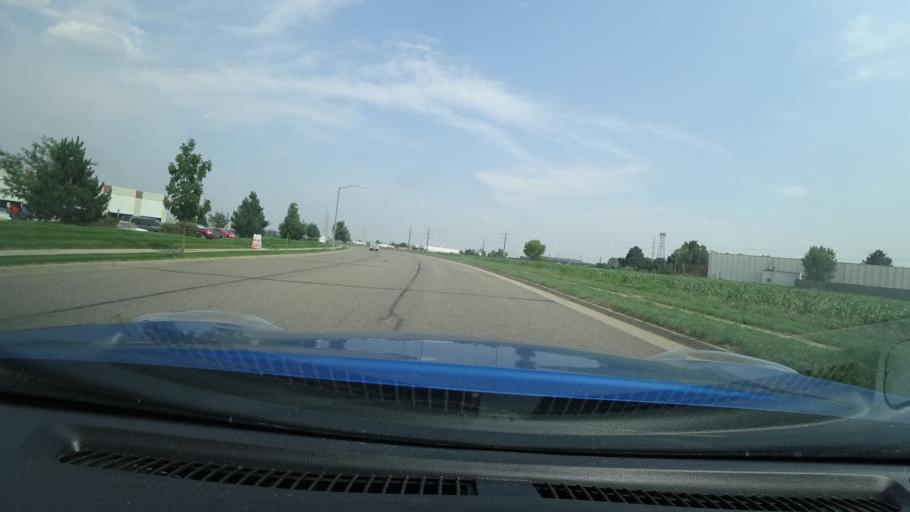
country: US
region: Colorado
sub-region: Adams County
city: Aurora
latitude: 39.7572
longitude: -104.7409
